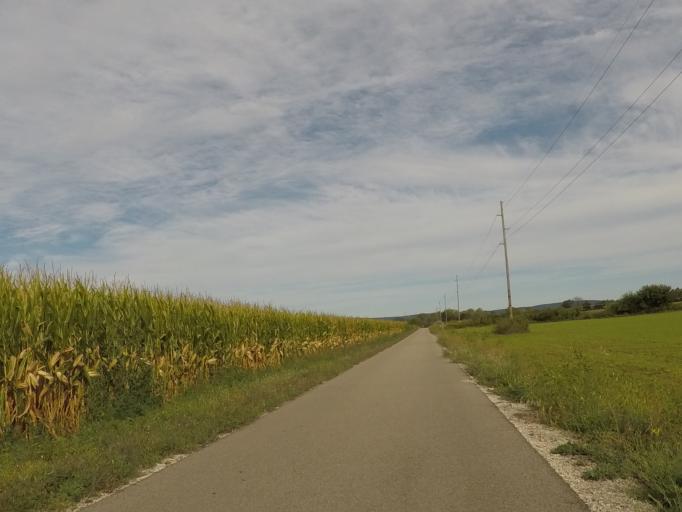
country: US
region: Wisconsin
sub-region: Sauk County
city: Prairie du Sac
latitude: 43.3209
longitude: -89.7416
